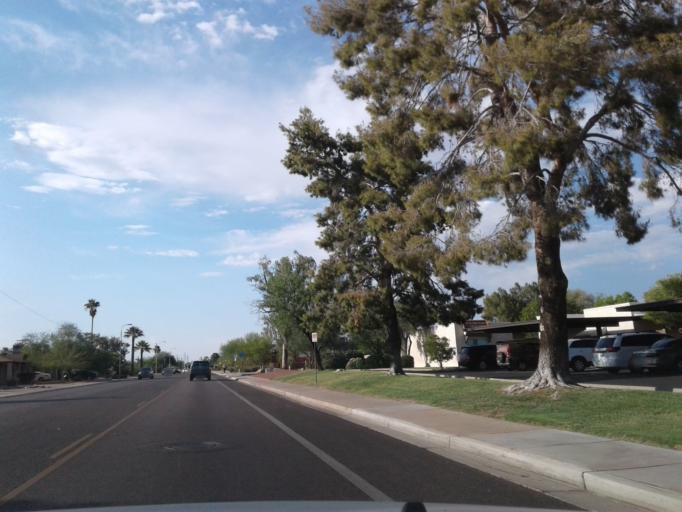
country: US
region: Arizona
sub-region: Maricopa County
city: Scottsdale
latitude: 33.4671
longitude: -111.9175
